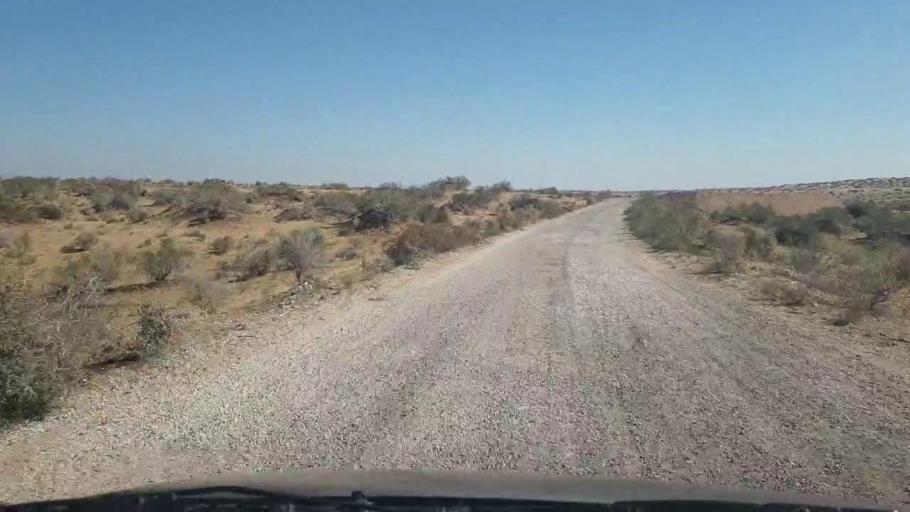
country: PK
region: Sindh
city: Bozdar
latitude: 27.0034
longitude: 68.8404
